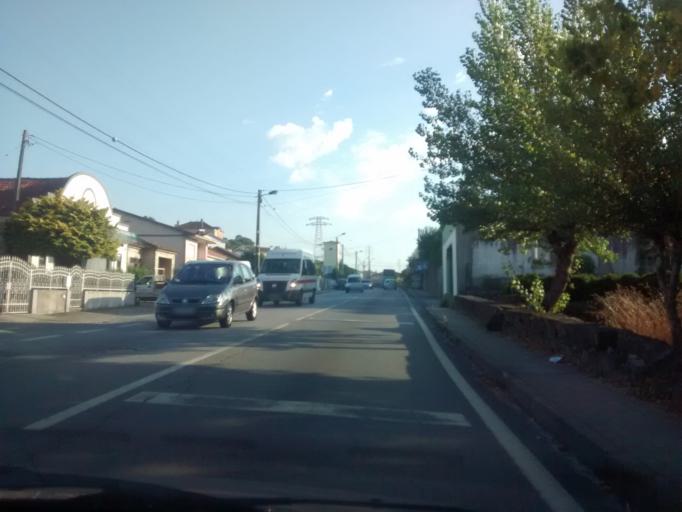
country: PT
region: Braga
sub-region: Braga
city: Adaufe
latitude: 41.5934
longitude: -8.4284
